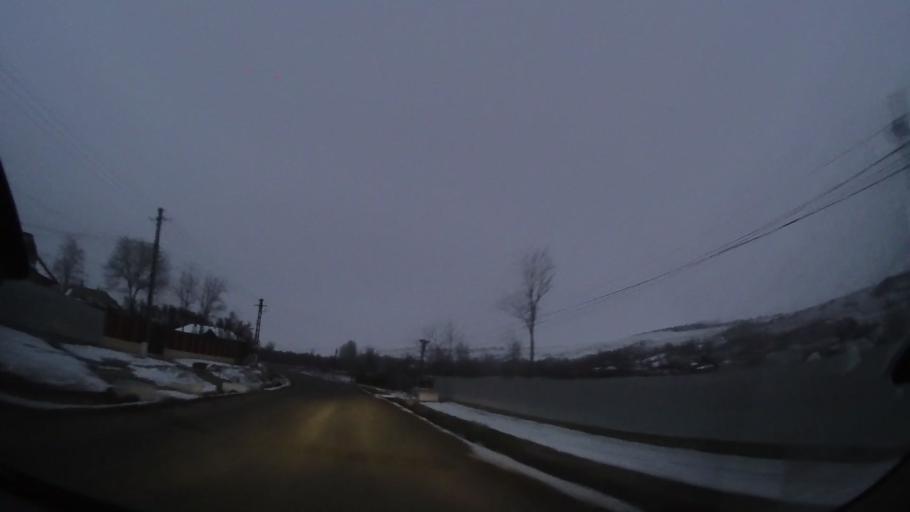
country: RO
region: Vaslui
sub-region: Comuna Dimitrie Cantemir
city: Dimitrie Cantemir
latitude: 46.5010
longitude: 28.0544
